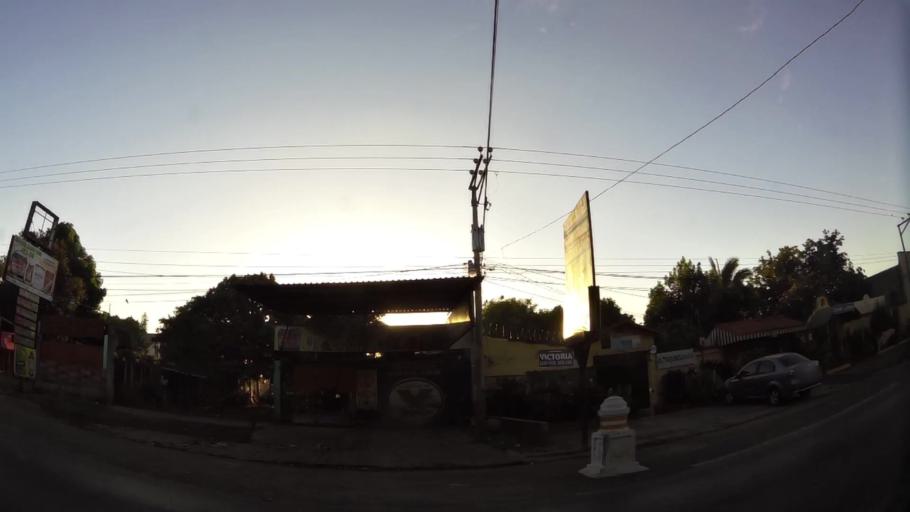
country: SV
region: Sonsonate
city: Sonzacate
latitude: 13.7311
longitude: -89.7139
